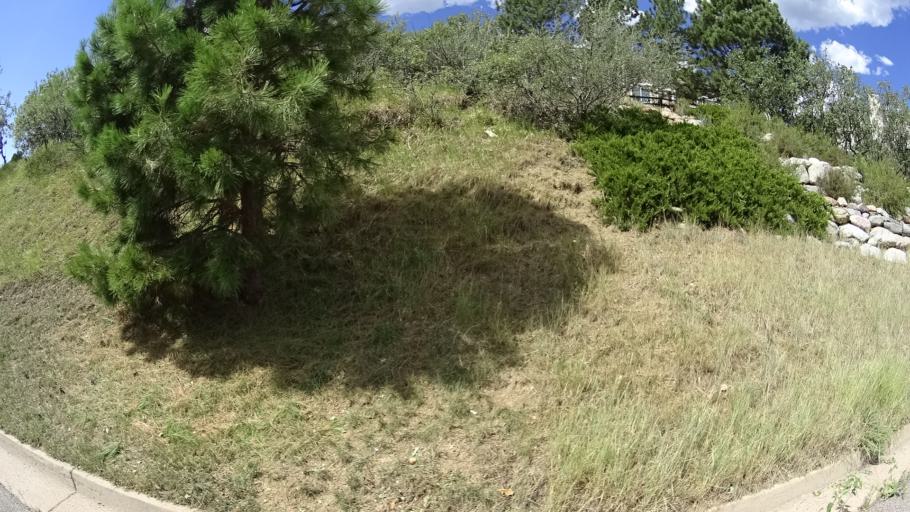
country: US
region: Colorado
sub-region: El Paso County
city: Fort Carson
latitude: 38.7624
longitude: -104.8221
